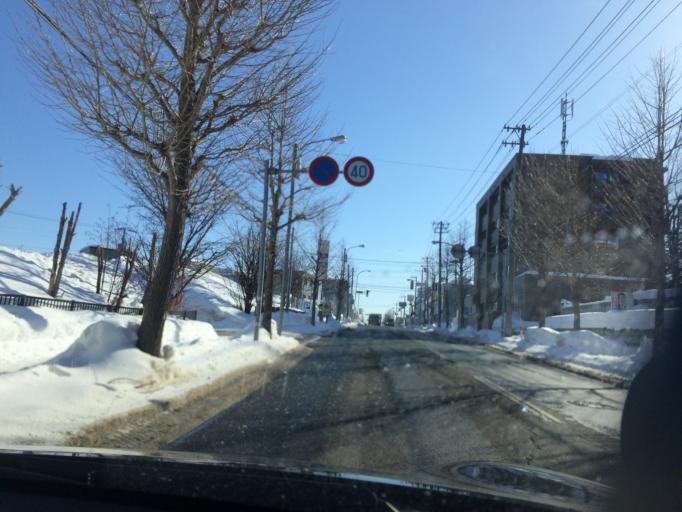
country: JP
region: Hokkaido
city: Sapporo
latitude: 43.0212
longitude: 141.4462
